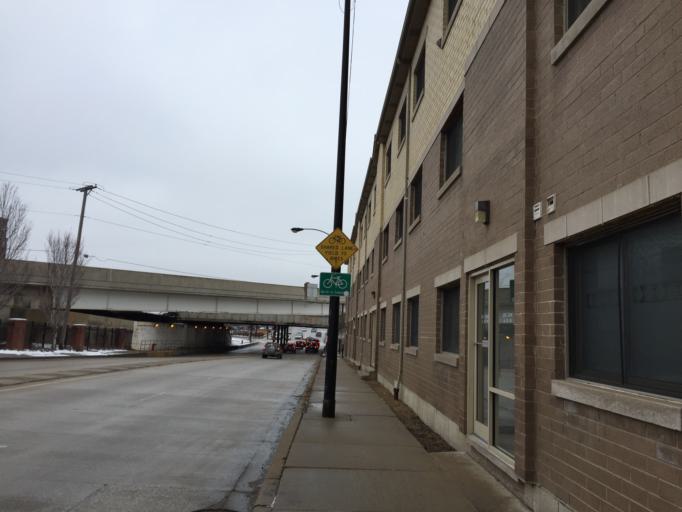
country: US
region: Illinois
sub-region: Cook County
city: Chicago
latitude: 41.8514
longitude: -87.6384
